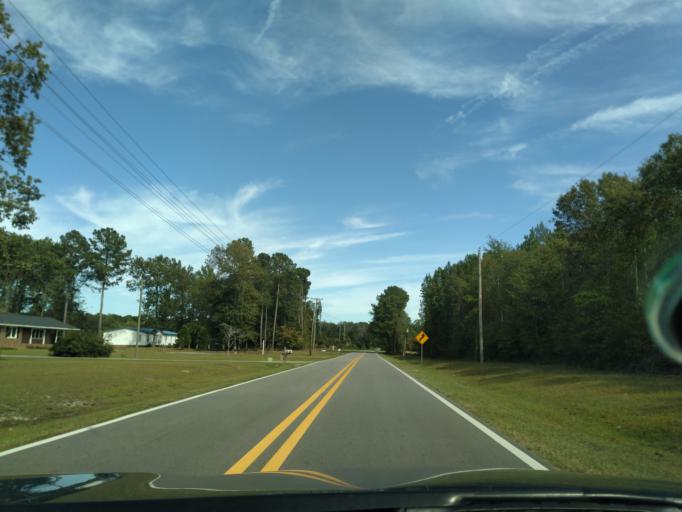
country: US
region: North Carolina
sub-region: Beaufort County
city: River Road
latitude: 35.5052
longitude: -76.9803
